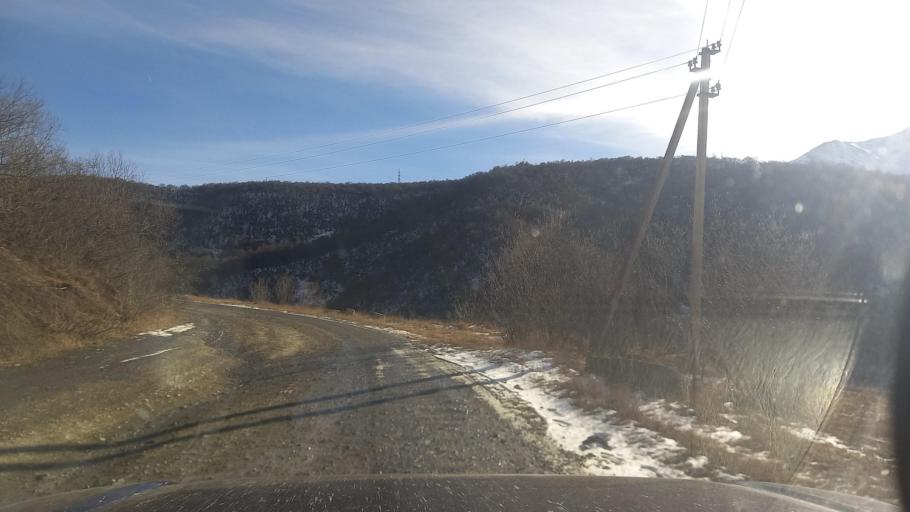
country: RU
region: North Ossetia
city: Verkhniy Fiagdon
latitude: 42.8368
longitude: 44.4679
